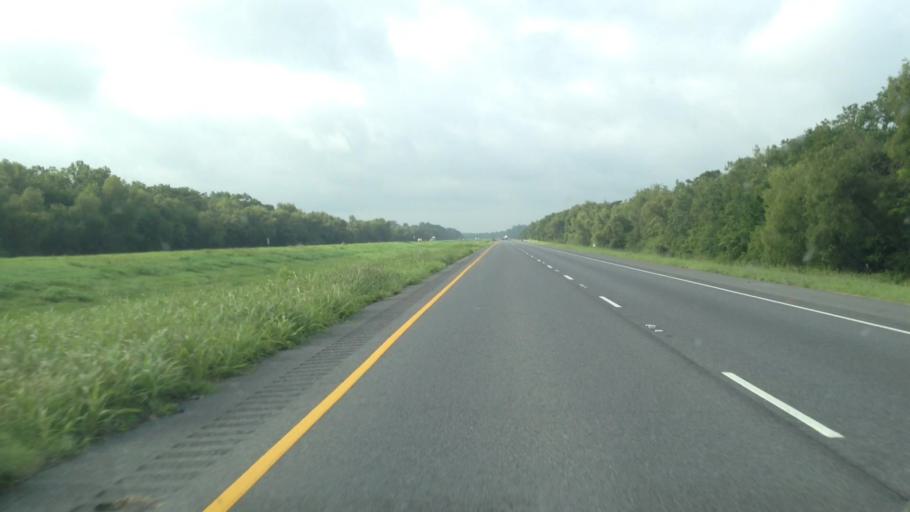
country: US
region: Louisiana
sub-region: Saint Landry Parish
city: Opelousas
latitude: 30.6890
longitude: -92.0796
